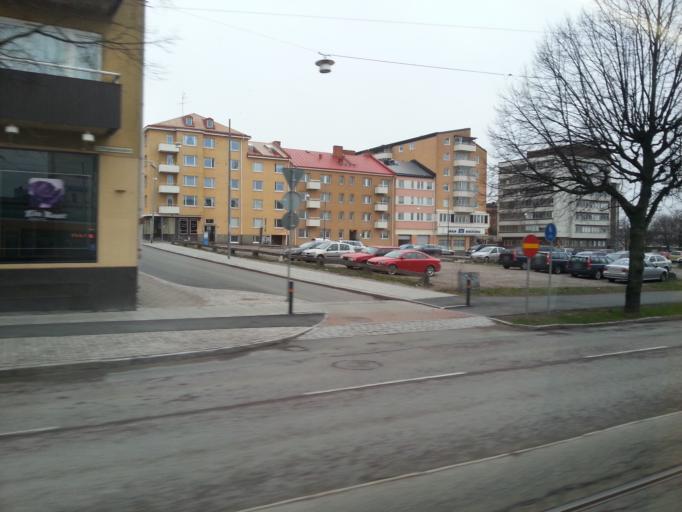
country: SE
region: OEstergoetland
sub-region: Norrkopings Kommun
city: Norrkoping
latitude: 58.5921
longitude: 16.1972
